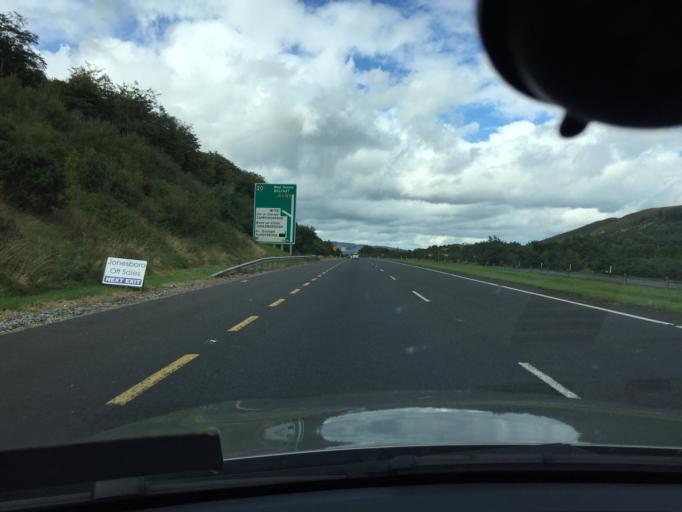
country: GB
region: Northern Ireland
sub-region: Newry and Mourne District
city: Newry
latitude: 54.0873
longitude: -6.3582
